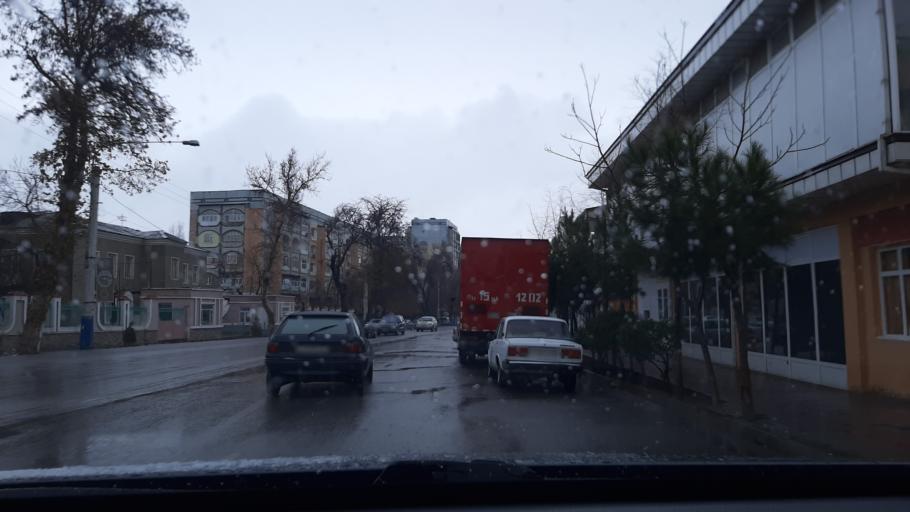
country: TJ
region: Viloyati Sughd
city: Khujand
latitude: 40.2752
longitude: 69.6411
